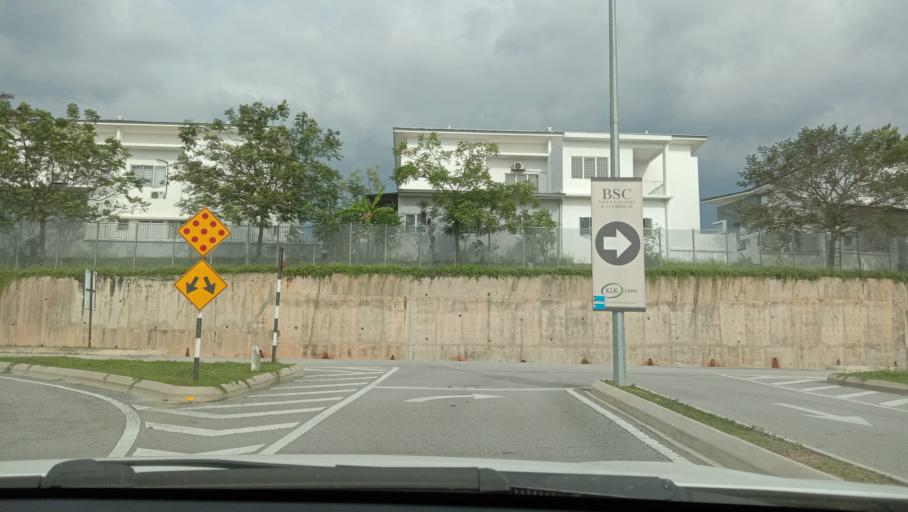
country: MY
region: Selangor
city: Ladang Seri Kundang
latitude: 3.2445
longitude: 101.4770
